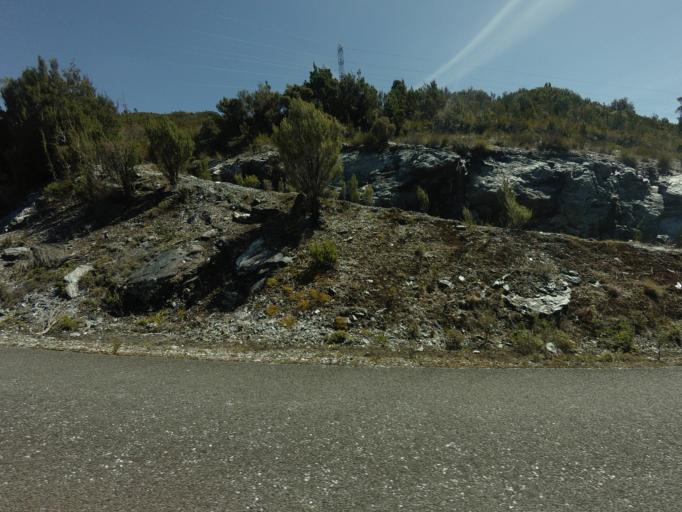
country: AU
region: Tasmania
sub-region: West Coast
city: Queenstown
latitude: -42.7475
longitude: 145.9812
